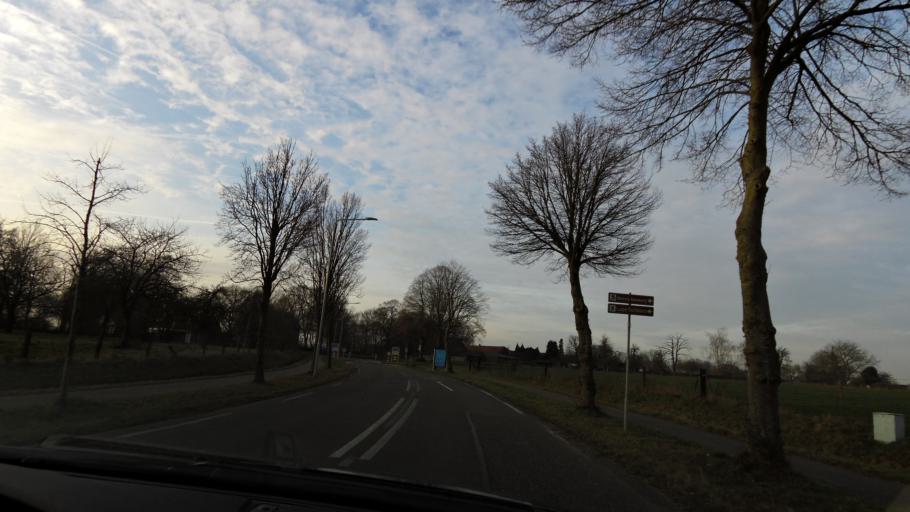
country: NL
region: Limburg
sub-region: Gemeente Beek
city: Beek
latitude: 50.9170
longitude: 5.8329
